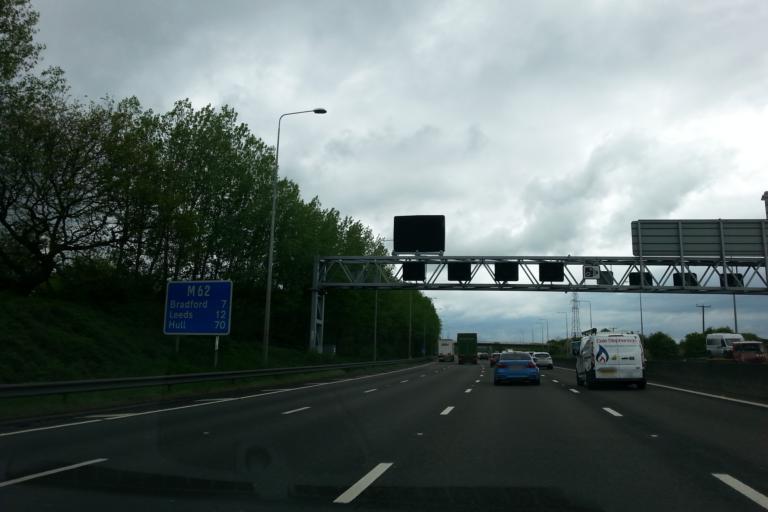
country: GB
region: England
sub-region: Kirklees
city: Cleckheaton
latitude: 53.7047
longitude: -1.7433
